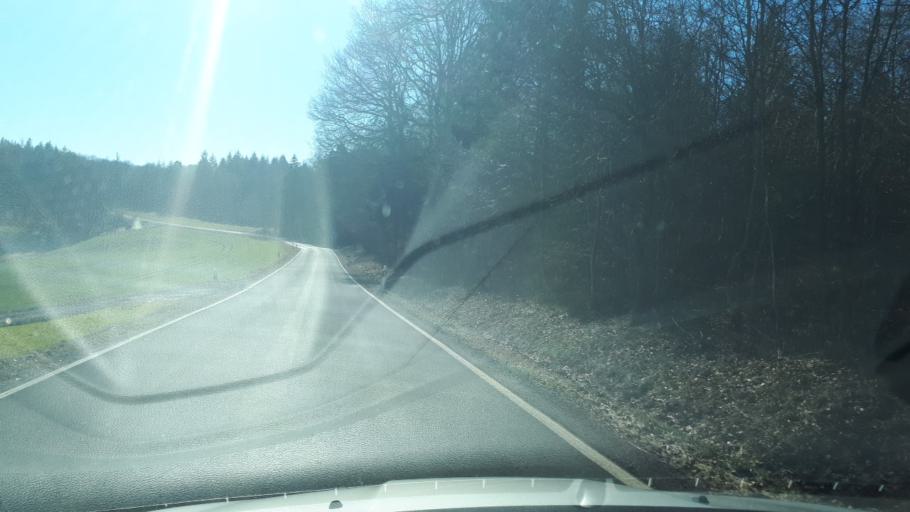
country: DE
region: Rheinland-Pfalz
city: Ellscheid
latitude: 50.1662
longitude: 6.9147
